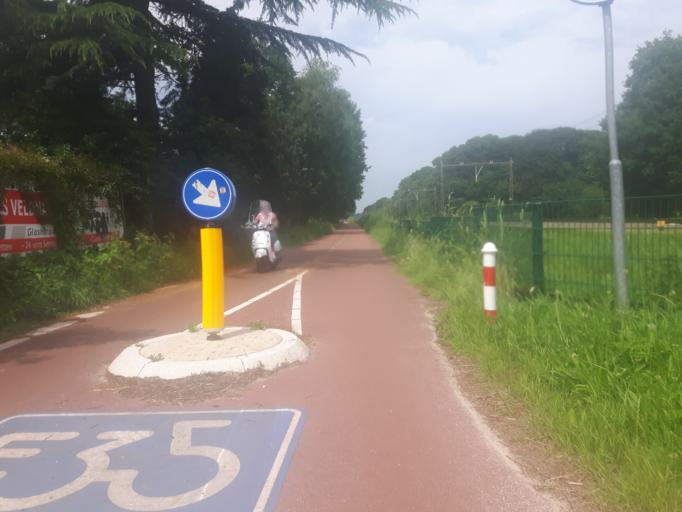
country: NL
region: Overijssel
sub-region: Gemeente Hengelo
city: Hengelo
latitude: 52.2480
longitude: 6.8216
